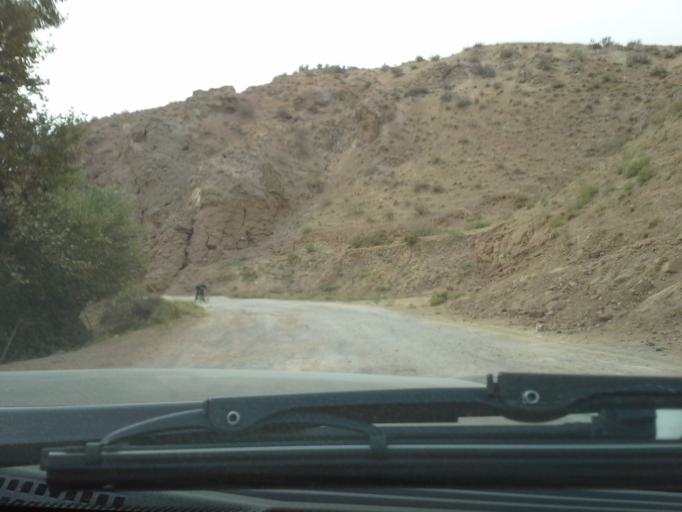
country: UZ
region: Qashqadaryo
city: Qorashina
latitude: 37.9387
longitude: 66.5359
